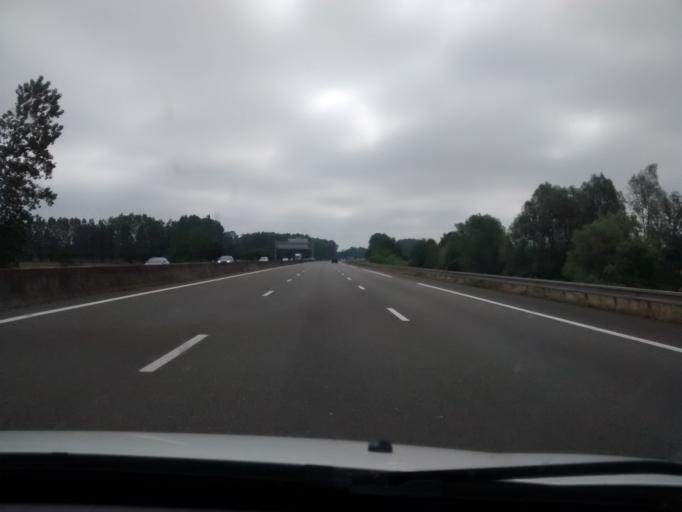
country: FR
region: Pays de la Loire
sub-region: Departement de la Sarthe
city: Champagne
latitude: 48.0519
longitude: 0.3155
